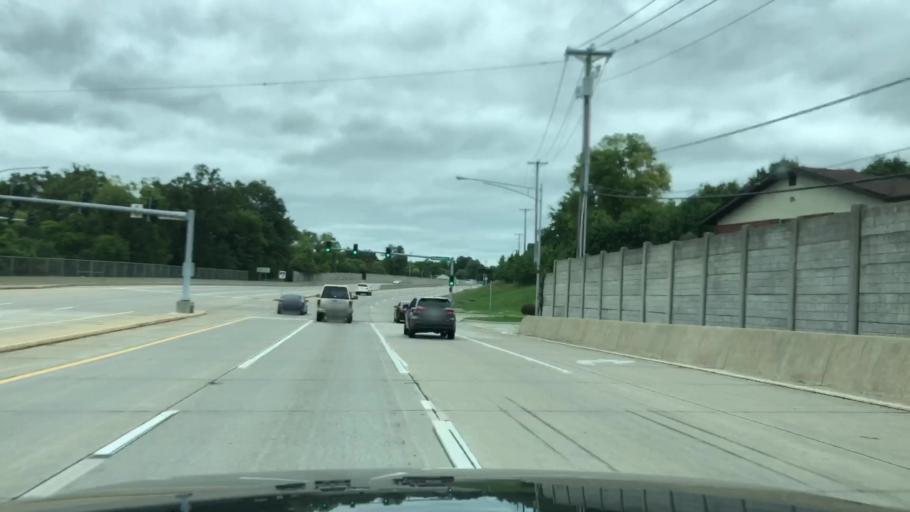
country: US
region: Missouri
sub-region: Saint Louis County
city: Manchester
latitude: 38.6092
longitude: -90.5113
